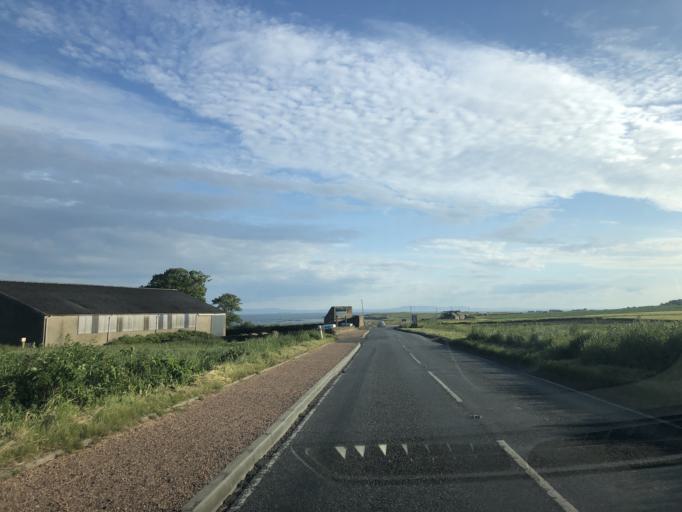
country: GB
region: Scotland
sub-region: Fife
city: Saint Monance
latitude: 56.1980
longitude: -2.7937
